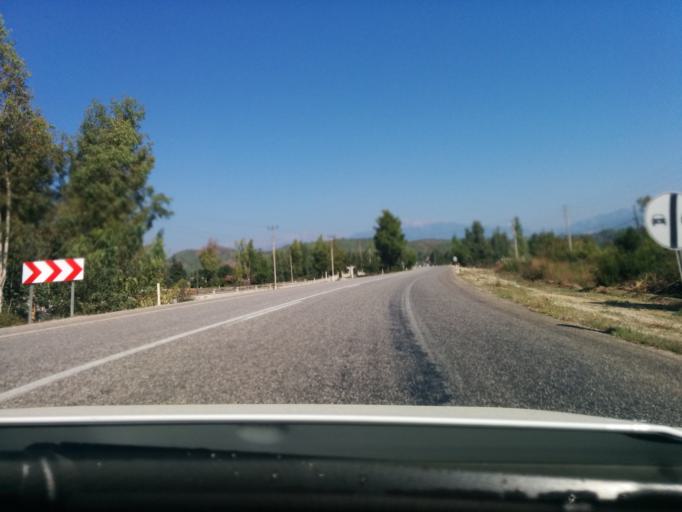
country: TR
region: Mugla
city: Kemer
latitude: 36.5854
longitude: 29.3502
